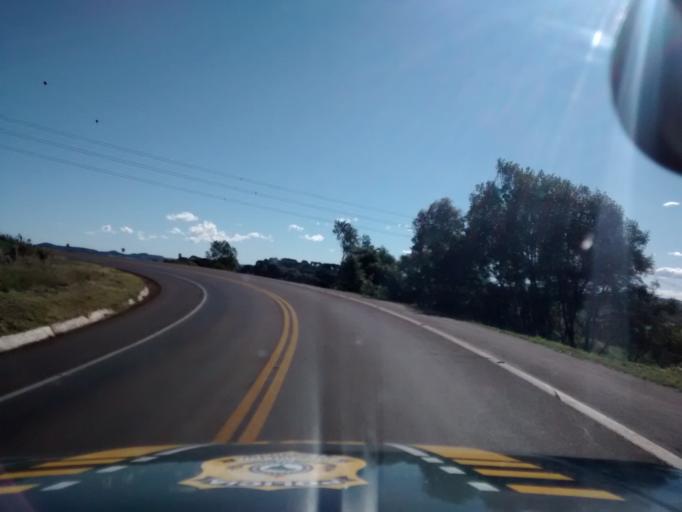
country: BR
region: Rio Grande do Sul
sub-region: Lagoa Vermelha
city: Lagoa Vermelha
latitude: -28.3334
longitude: -51.2984
